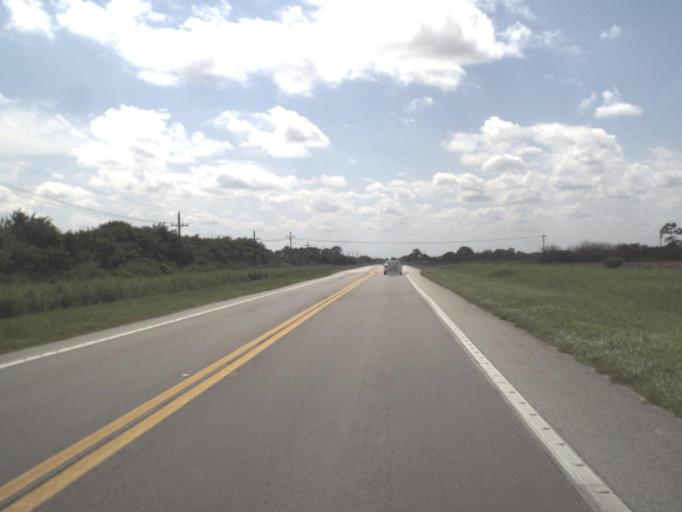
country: US
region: Florida
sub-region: Hendry County
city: Port LaBelle
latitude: 26.6492
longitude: -81.4362
